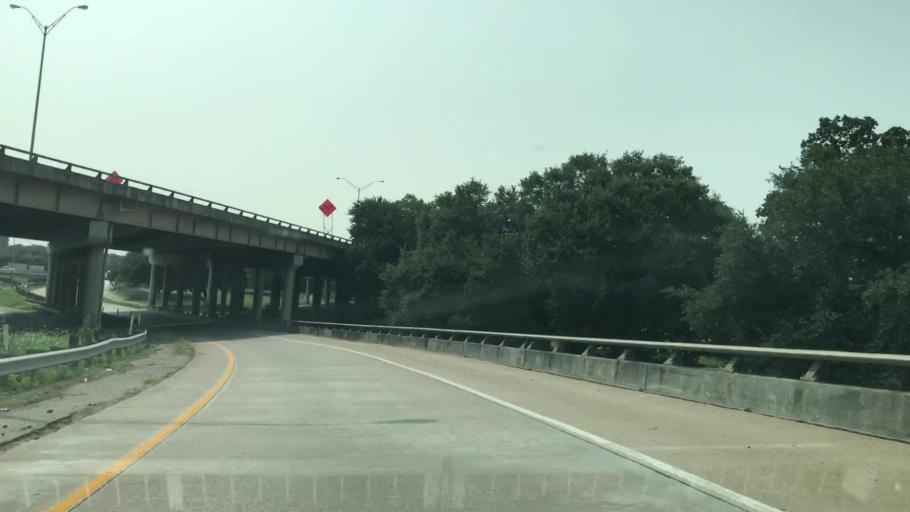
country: US
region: Texas
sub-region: Dallas County
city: Dallas
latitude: 32.7662
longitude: -96.7770
